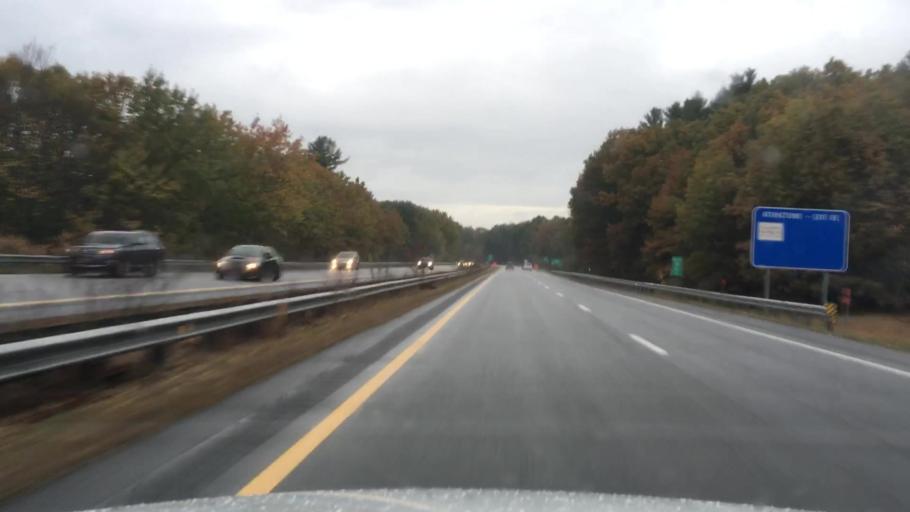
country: US
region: New Hampshire
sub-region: Strafford County
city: Dover
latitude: 43.1689
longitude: -70.8597
